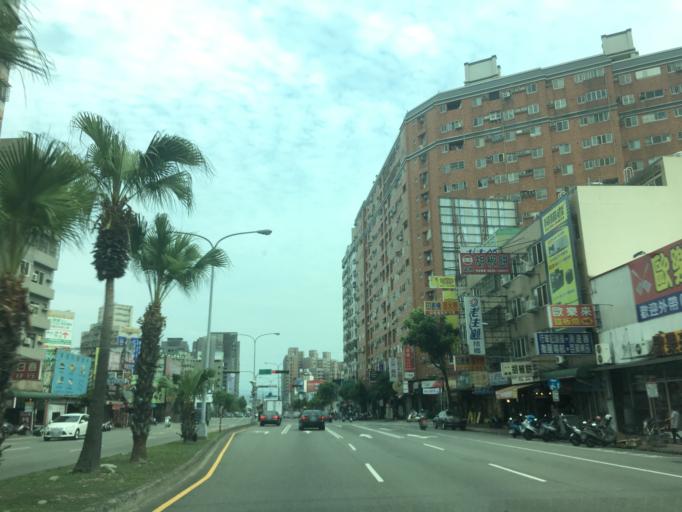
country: TW
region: Taiwan
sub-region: Taichung City
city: Taichung
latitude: 24.1145
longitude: 120.6559
